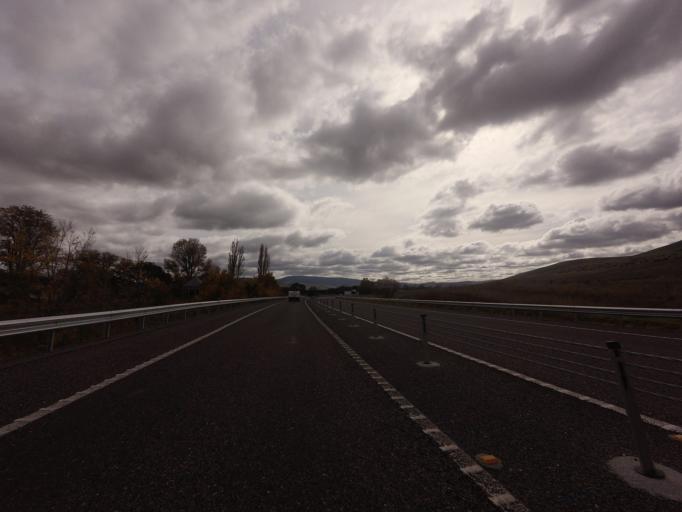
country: AU
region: Tasmania
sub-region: Brighton
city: Bridgewater
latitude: -42.5210
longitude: 147.1936
